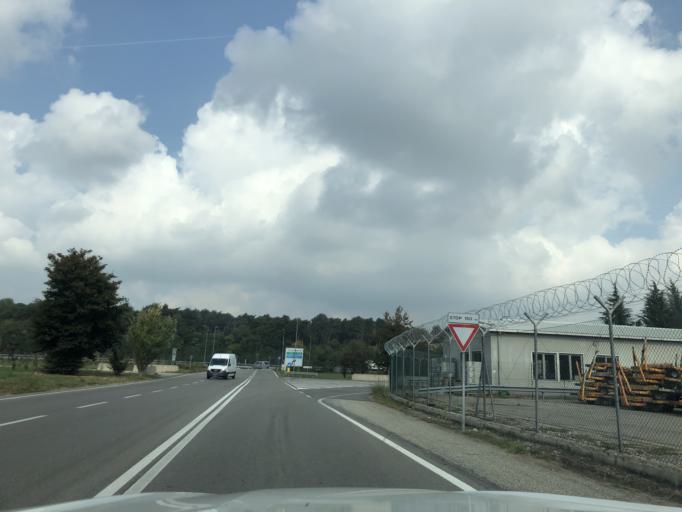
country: IT
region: Lombardy
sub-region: Provincia di Varese
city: Vizzola Ticino
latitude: 45.6468
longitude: 8.7112
